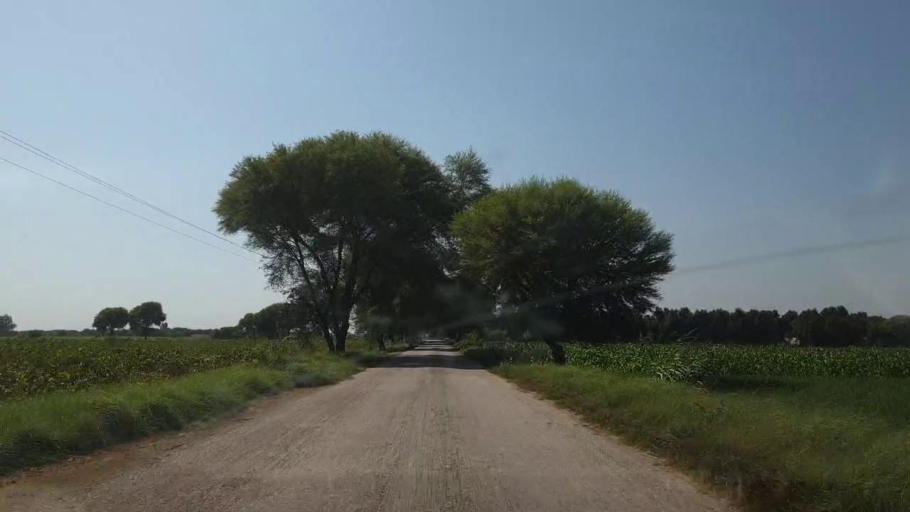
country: PK
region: Sindh
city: Tando Jam
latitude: 25.3918
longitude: 68.5845
